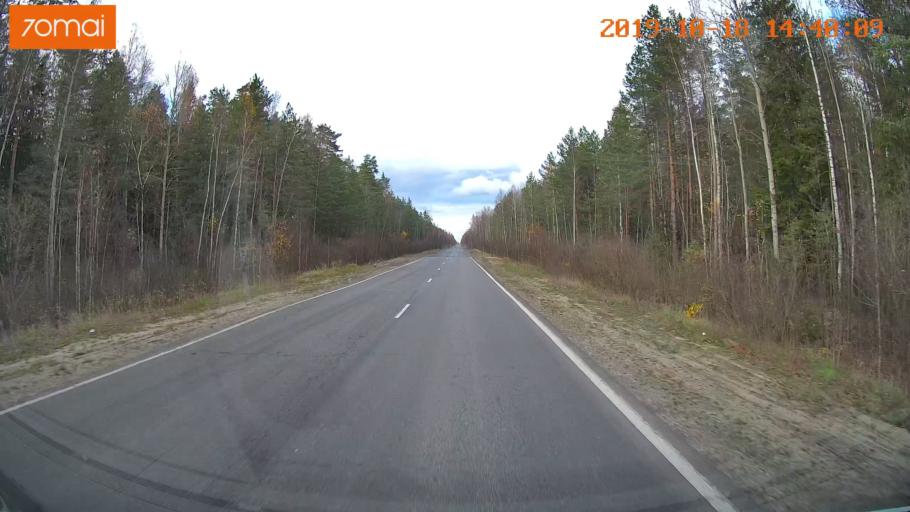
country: RU
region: Vladimir
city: Velikodvorskiy
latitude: 55.2722
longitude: 40.6684
